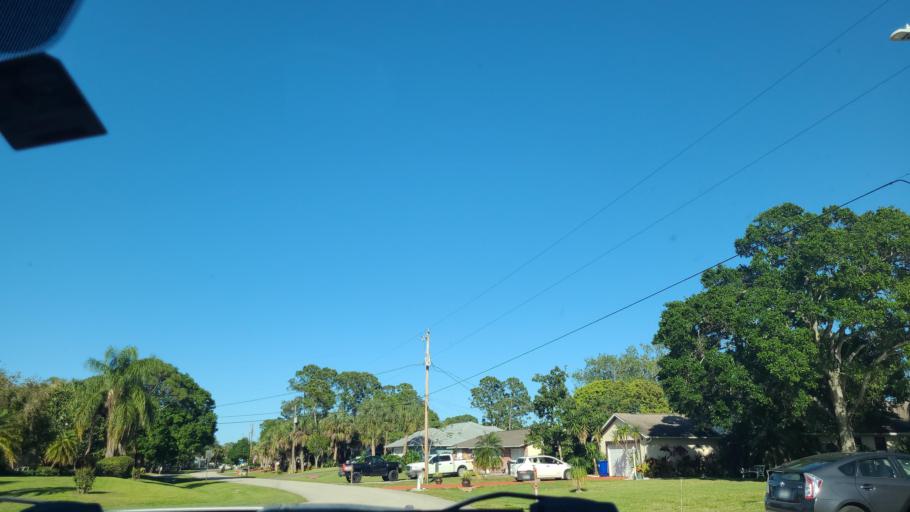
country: US
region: Florida
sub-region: Indian River County
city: Sebastian
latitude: 27.7964
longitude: -80.4914
